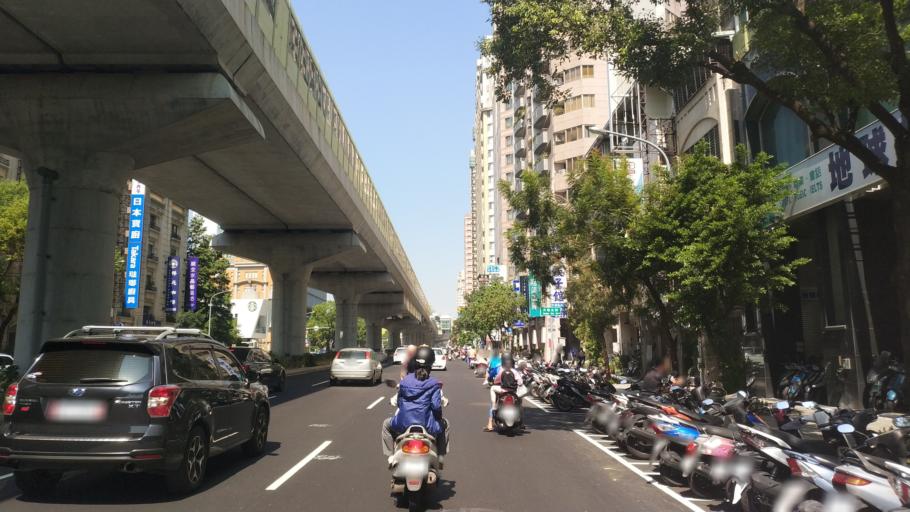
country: TW
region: Taiwan
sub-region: Taichung City
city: Taichung
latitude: 24.1413
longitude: 120.6469
